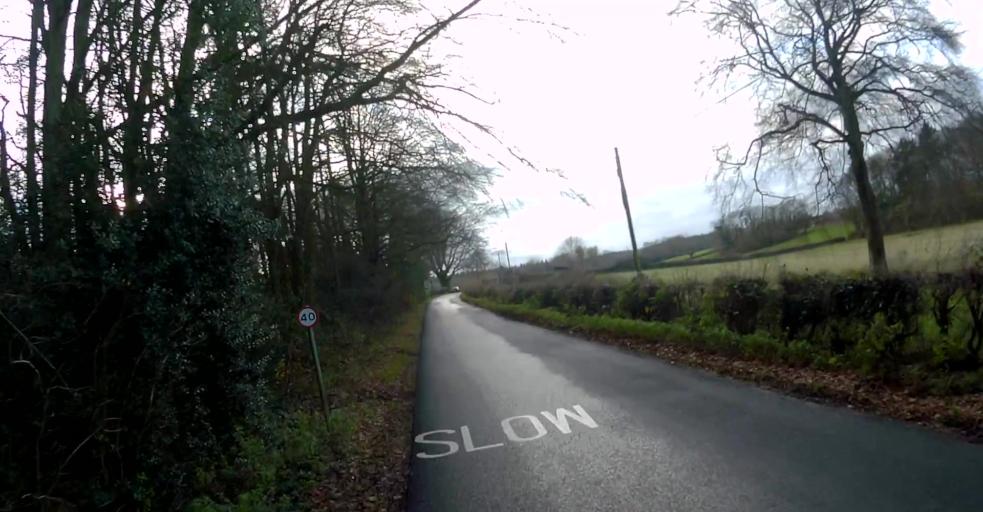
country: GB
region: England
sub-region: Hampshire
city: Old Basing
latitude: 51.1998
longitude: -1.0504
